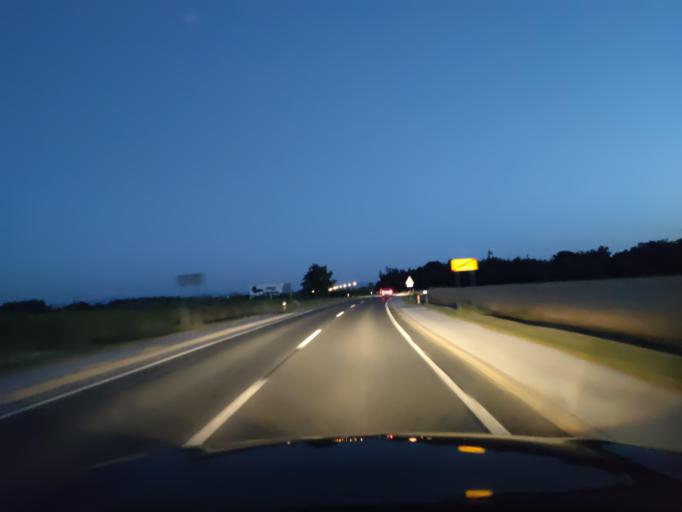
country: HR
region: Medimurska
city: Mackovec
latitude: 46.4224
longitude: 16.4276
